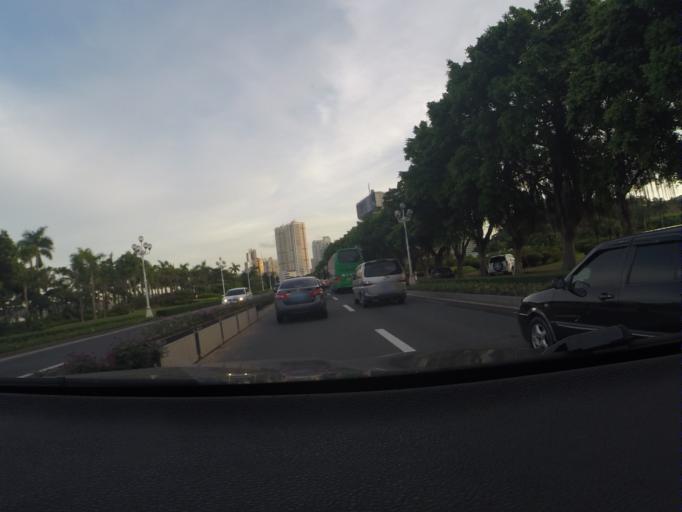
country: CN
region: Guangdong
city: Zhuhai
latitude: 22.2997
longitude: 113.5735
